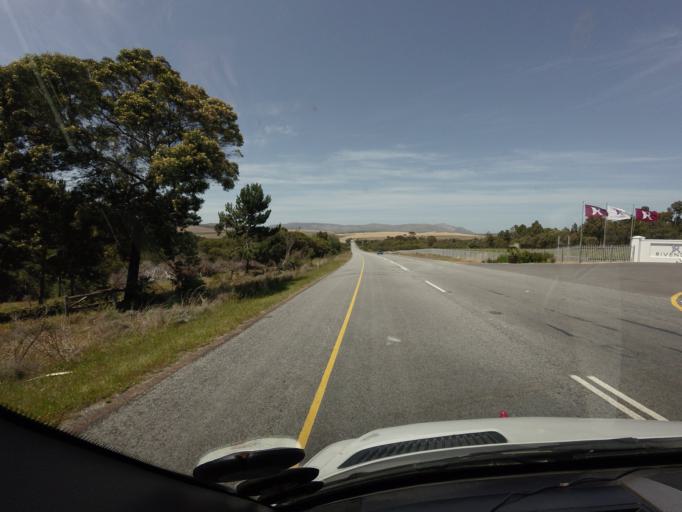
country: ZA
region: Western Cape
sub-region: Overberg District Municipality
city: Hermanus
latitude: -34.3032
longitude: 19.1441
